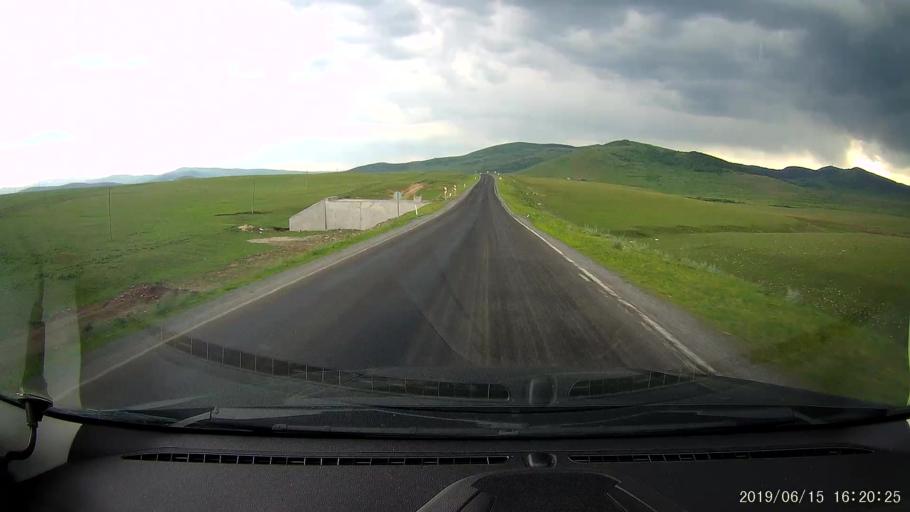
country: TR
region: Ardahan
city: Hanak
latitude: 41.2145
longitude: 42.8487
